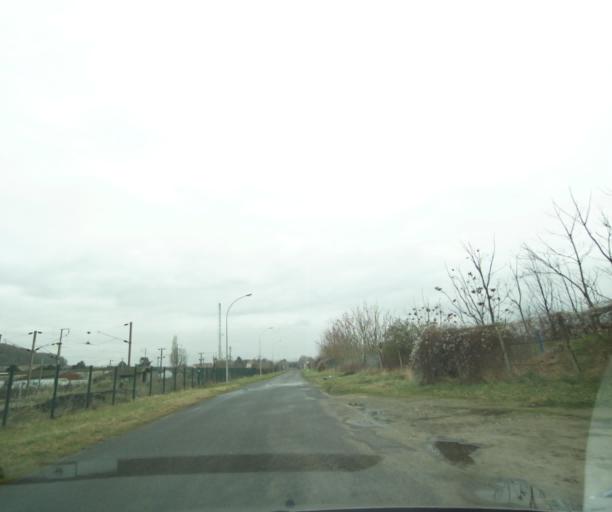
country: FR
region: Picardie
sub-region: Departement de l'Oise
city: Noyon
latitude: 49.5771
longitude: 3.0152
